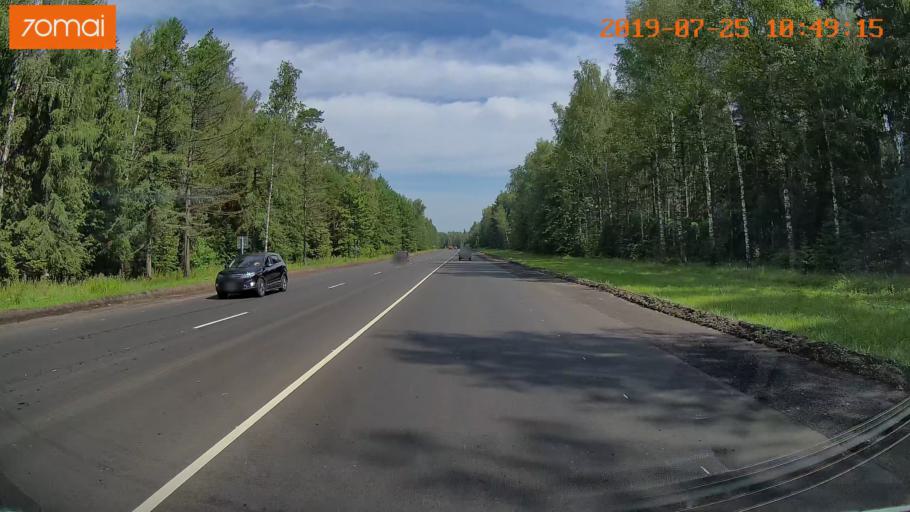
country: RU
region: Ivanovo
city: Bogorodskoye
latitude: 57.0735
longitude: 40.9926
